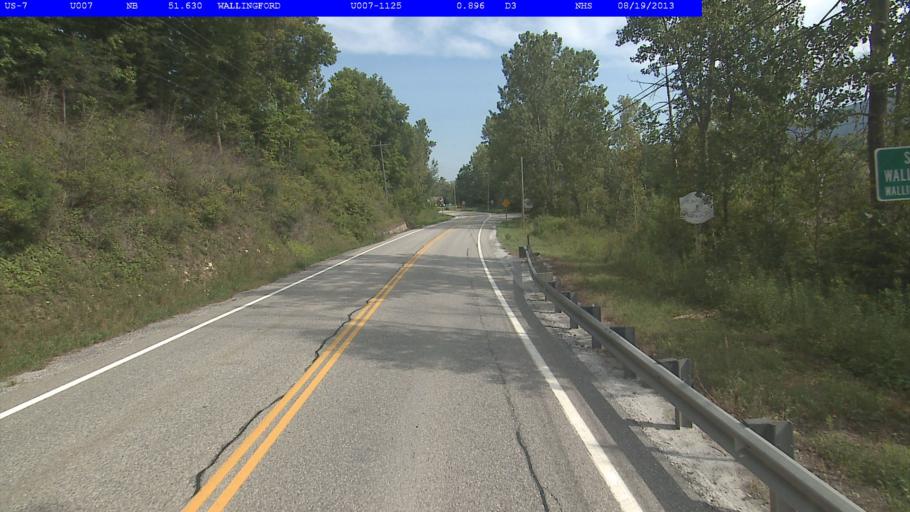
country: US
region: Vermont
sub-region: Rutland County
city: West Rutland
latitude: 43.4093
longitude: -72.9931
